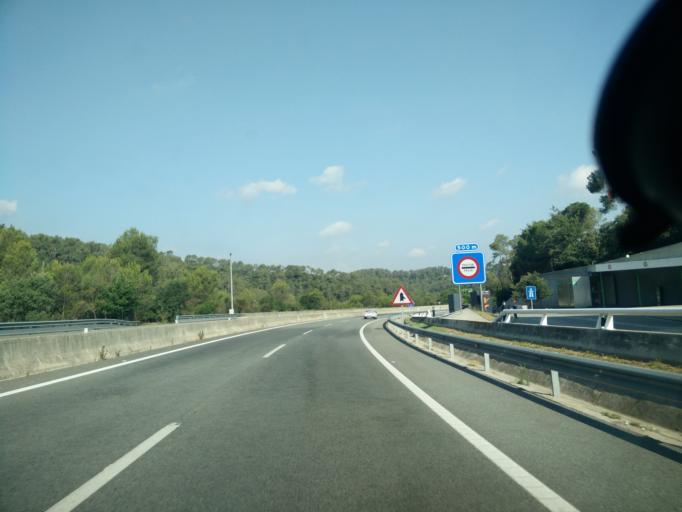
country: ES
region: Catalonia
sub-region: Provincia de Barcelona
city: Sant Cugat del Valles
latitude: 41.4333
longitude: 2.0780
